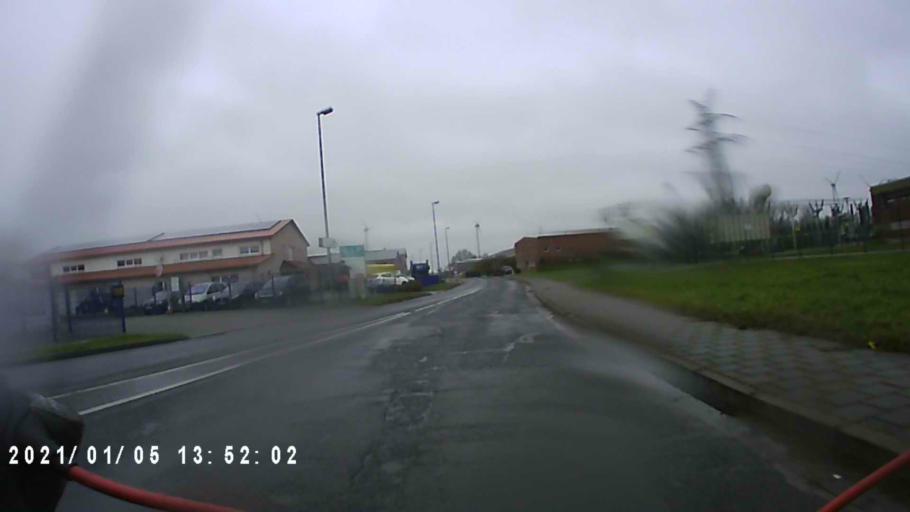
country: DE
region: Lower Saxony
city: Weener
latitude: 53.1726
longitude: 7.3596
